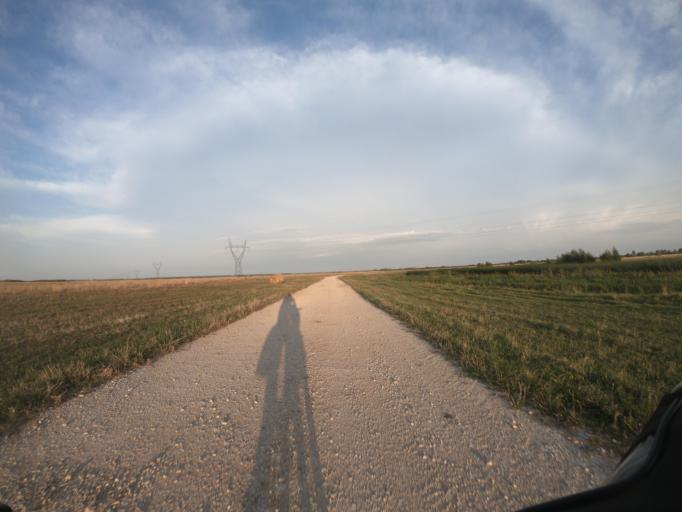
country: HU
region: Jasz-Nagykun-Szolnok
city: Tiszafured
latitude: 47.7308
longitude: 20.7950
